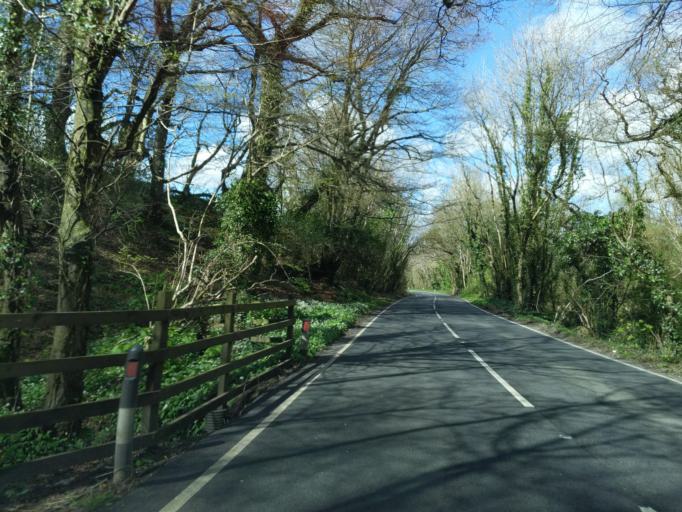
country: GB
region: England
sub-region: Cornwall
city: Helland
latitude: 50.5015
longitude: -4.7761
